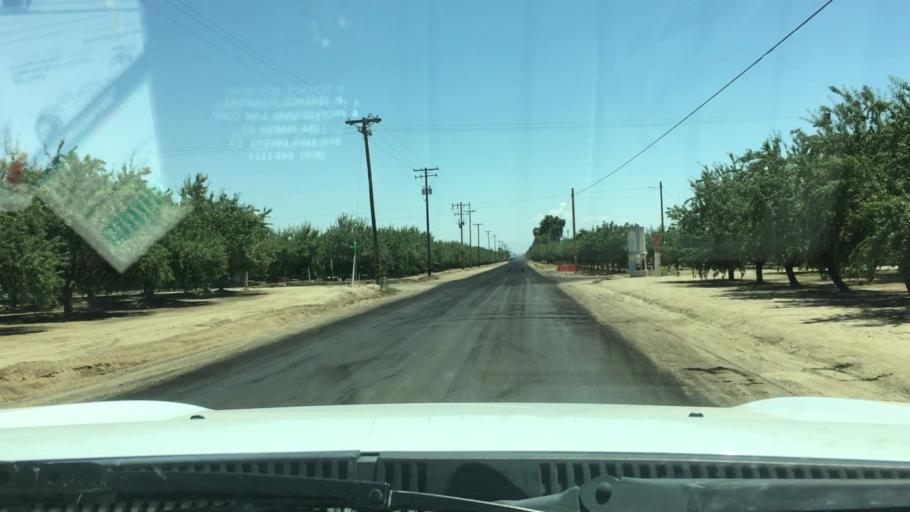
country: US
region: California
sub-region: Kern County
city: Wasco
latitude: 35.5290
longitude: -119.3328
